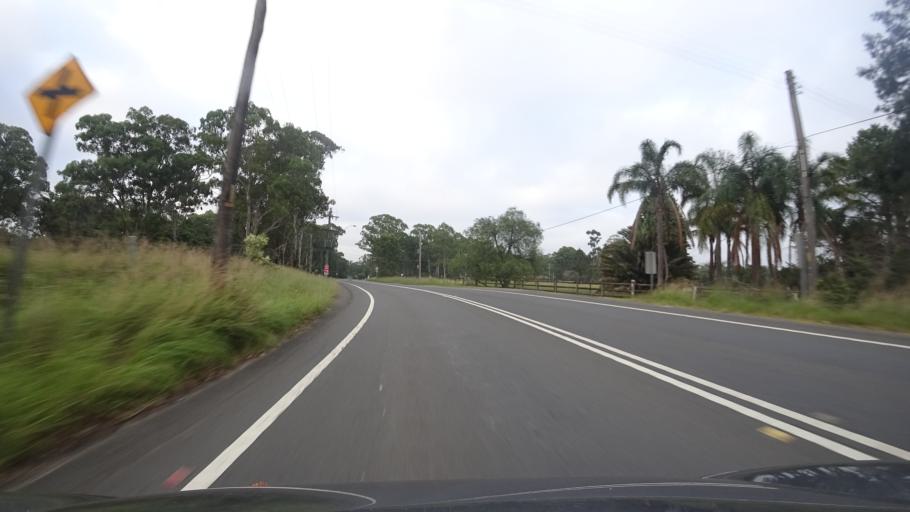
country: AU
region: New South Wales
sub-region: Blacktown
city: Rouse Hill
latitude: -33.6601
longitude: 150.9245
